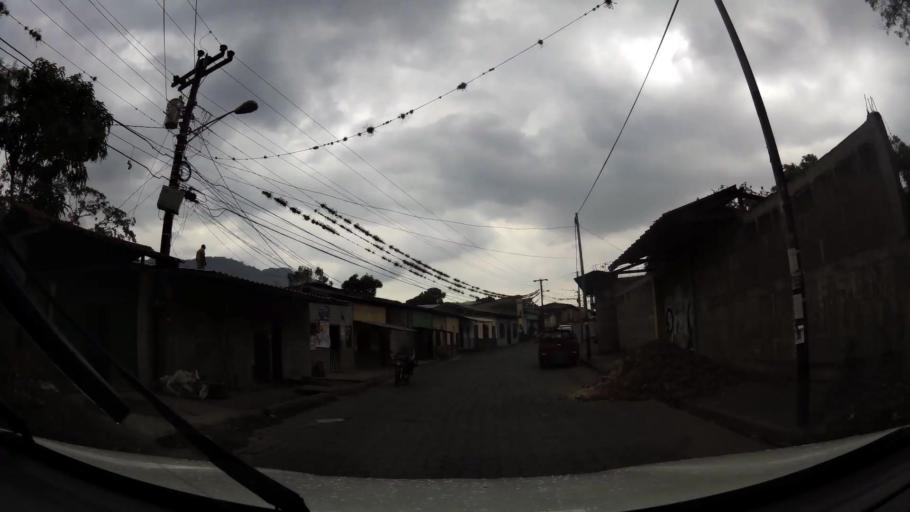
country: NI
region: Jinotega
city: Jinotega
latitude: 13.0990
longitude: -86.0026
